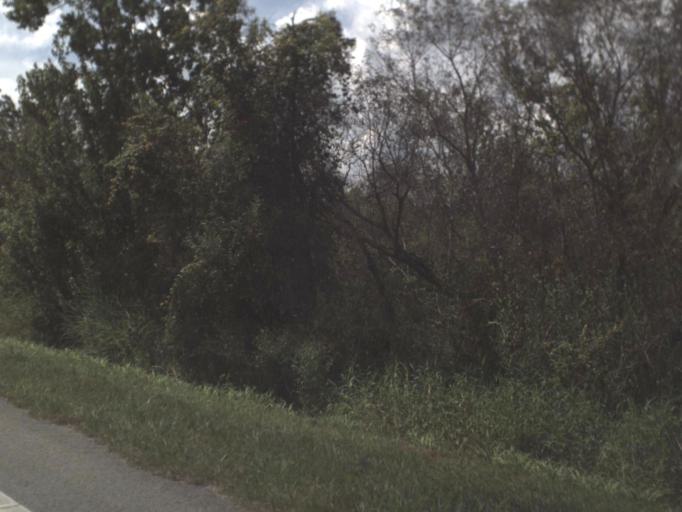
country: US
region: Florida
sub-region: Collier County
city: Immokalee
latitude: 26.2114
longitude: -81.3457
